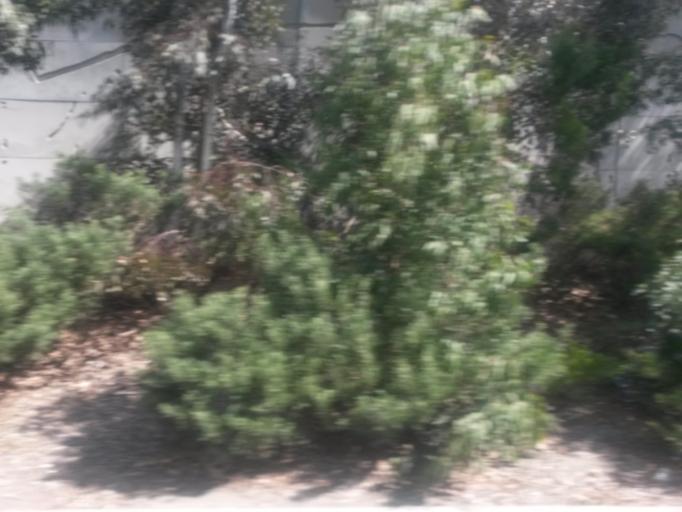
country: AU
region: Victoria
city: Glenferrie
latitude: -37.8404
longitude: 145.0390
